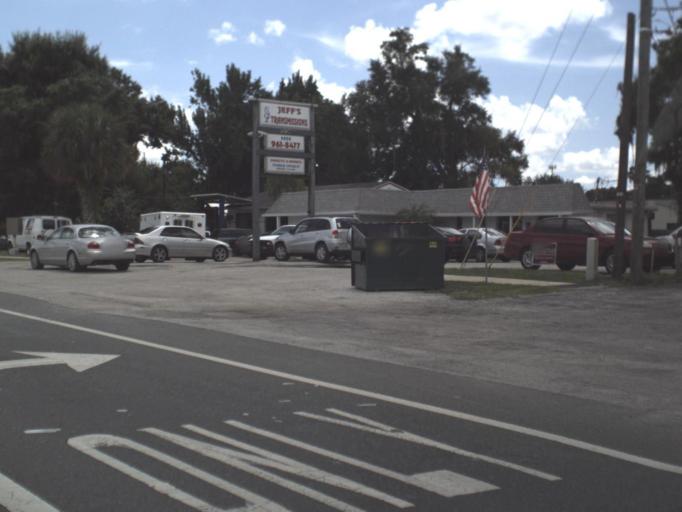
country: US
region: Florida
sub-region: Hillsborough County
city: Carrollwood
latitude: 28.0395
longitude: -82.5050
